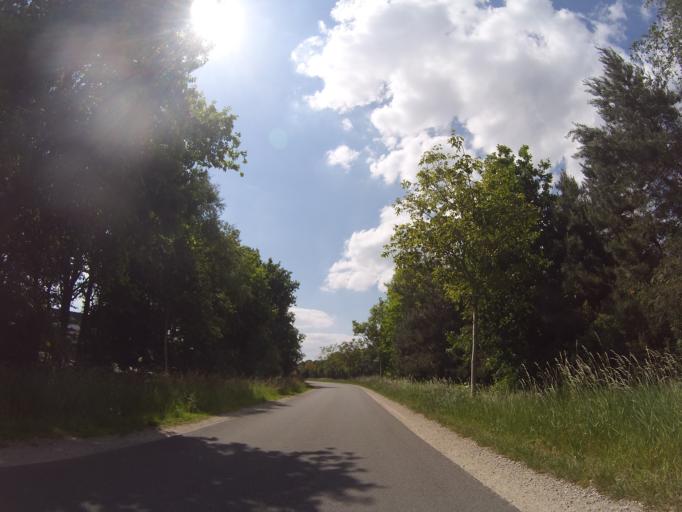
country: NL
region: Gelderland
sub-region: Gemeente Barneveld
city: Stroe
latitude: 52.1868
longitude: 5.6762
